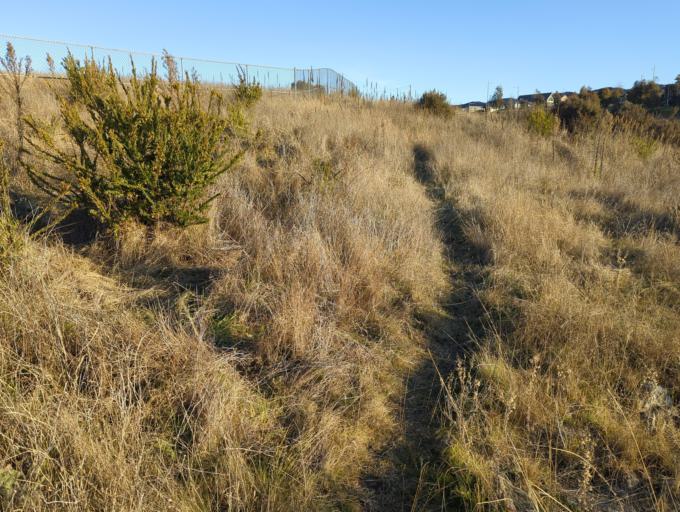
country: AU
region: New South Wales
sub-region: Queanbeyan
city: Queanbeyan
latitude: -35.4267
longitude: 149.2442
